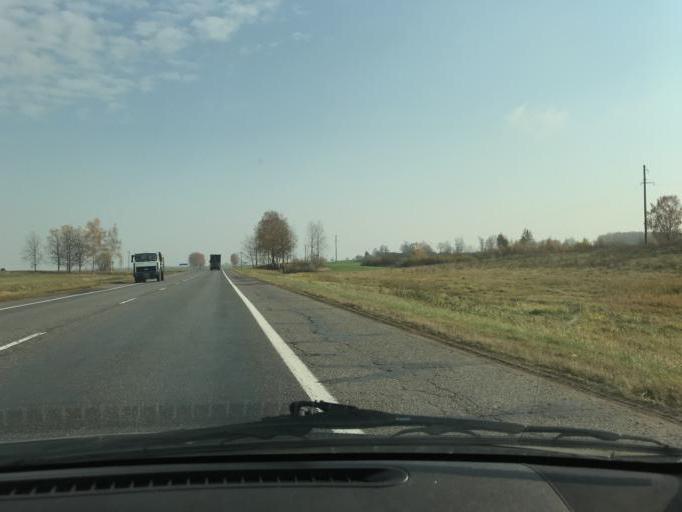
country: BY
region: Vitebsk
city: Chashniki
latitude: 55.0133
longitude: 29.0996
